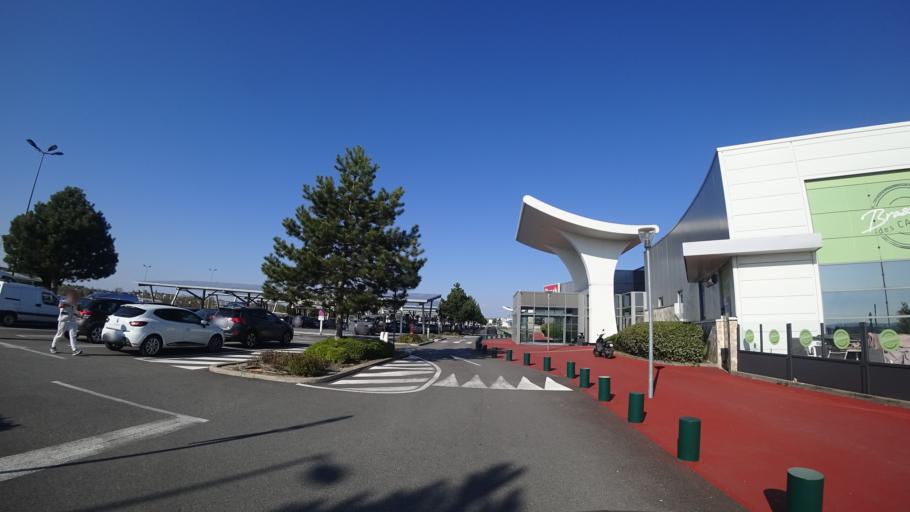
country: FR
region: Midi-Pyrenees
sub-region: Departement de l'Aveyron
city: Sebazac-Concoures
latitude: 44.3918
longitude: 2.6008
